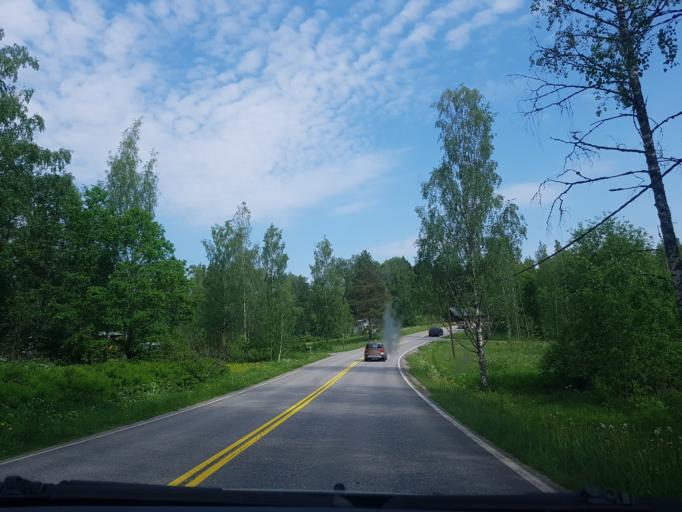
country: FI
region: Uusimaa
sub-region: Helsinki
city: Vihti
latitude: 60.3067
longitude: 24.3989
